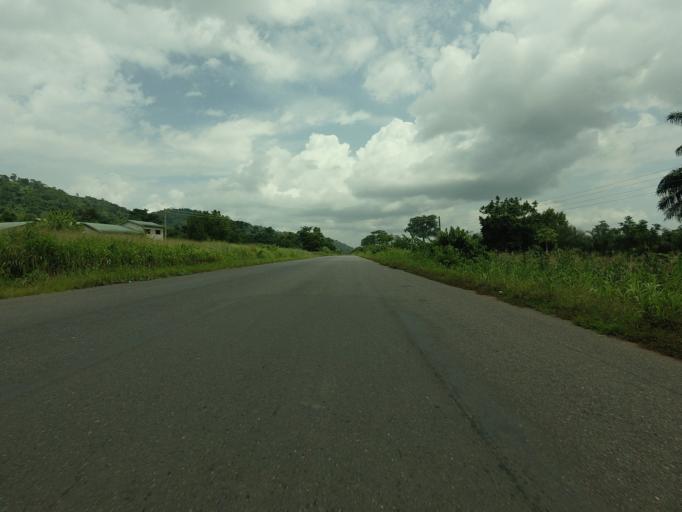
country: GH
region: Volta
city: Ho
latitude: 6.4929
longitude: 0.2016
